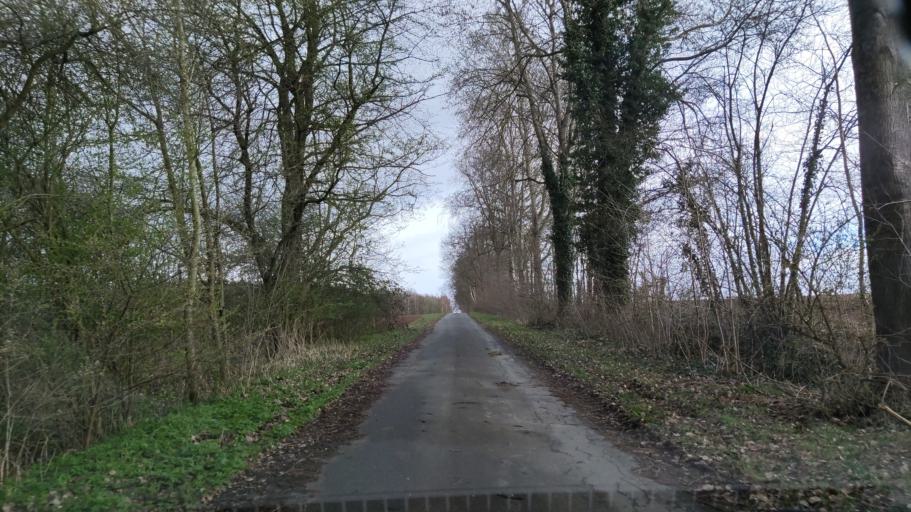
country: DE
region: Lower Saxony
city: Thomasburg
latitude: 53.2000
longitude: 10.6830
